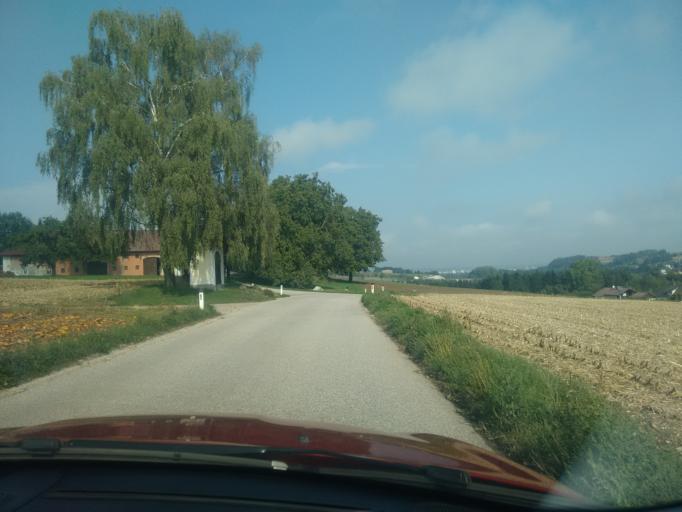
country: AT
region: Upper Austria
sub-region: Wels-Land
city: Steinhaus
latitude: 48.1159
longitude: 14.0075
